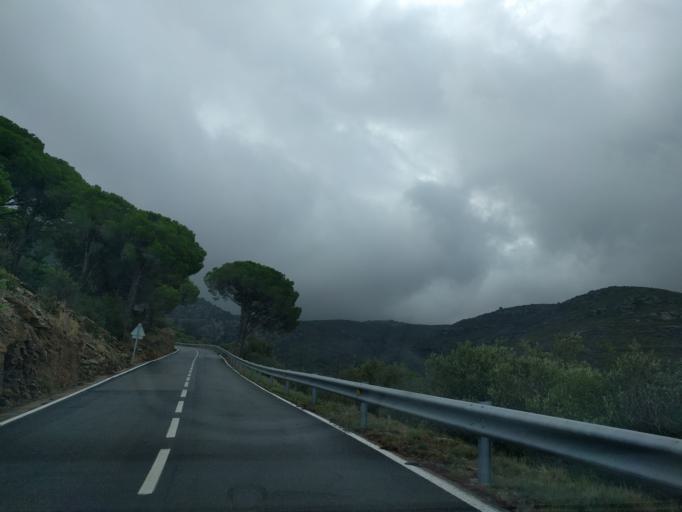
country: ES
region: Catalonia
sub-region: Provincia de Girona
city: Cadaques
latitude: 42.3074
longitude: 3.2206
